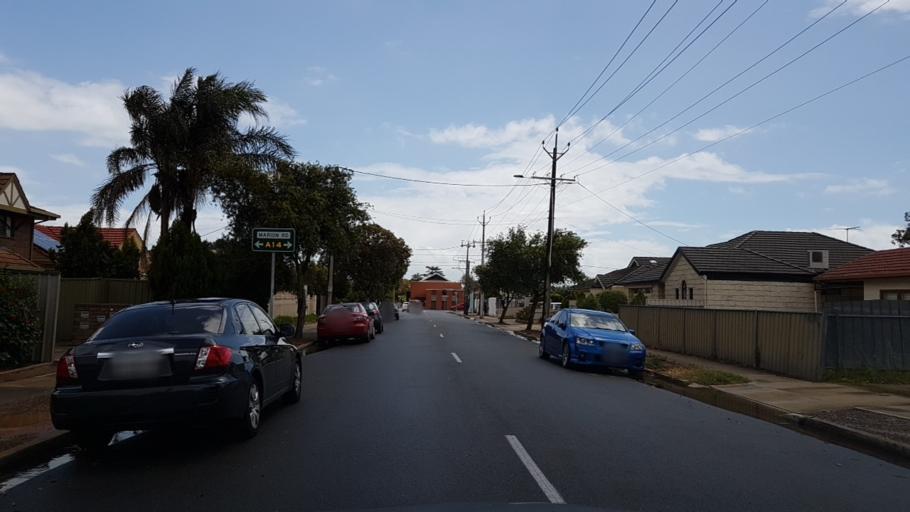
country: AU
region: South Australia
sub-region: Marion
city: South Plympton
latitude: -34.9869
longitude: 138.5580
